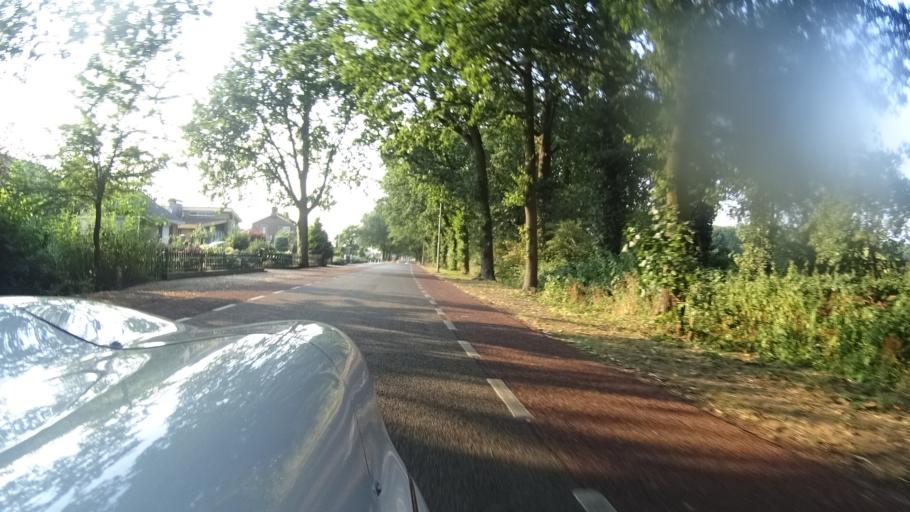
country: NL
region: Gelderland
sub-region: Gemeente Druten
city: Druten
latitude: 51.8335
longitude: 5.5871
